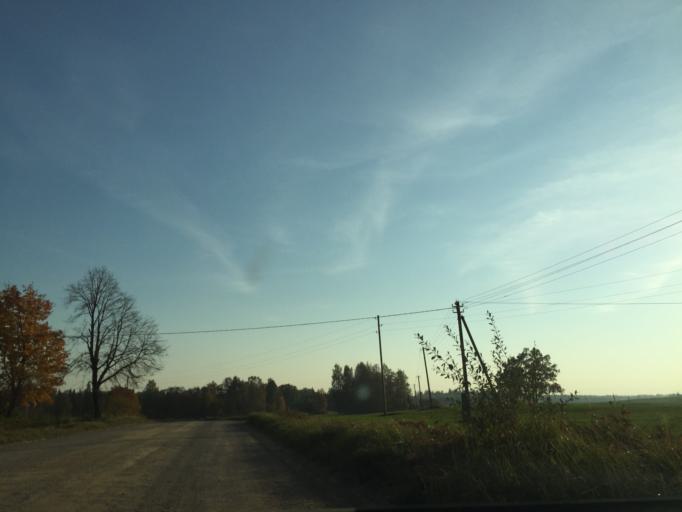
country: LV
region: Vainode
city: Vainode
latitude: 56.6078
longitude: 21.8232
